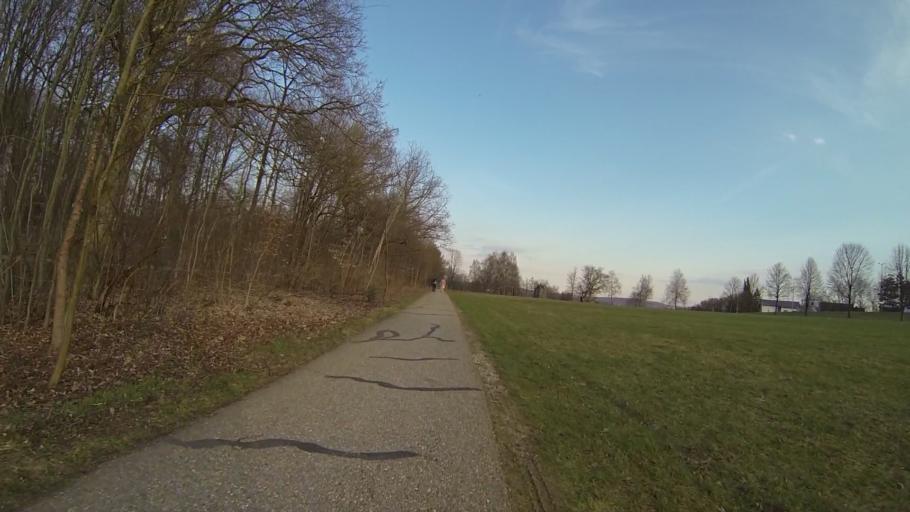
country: DE
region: Baden-Wuerttemberg
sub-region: Regierungsbezirk Stuttgart
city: Heidenheim an der Brenz
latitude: 48.6925
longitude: 10.1390
